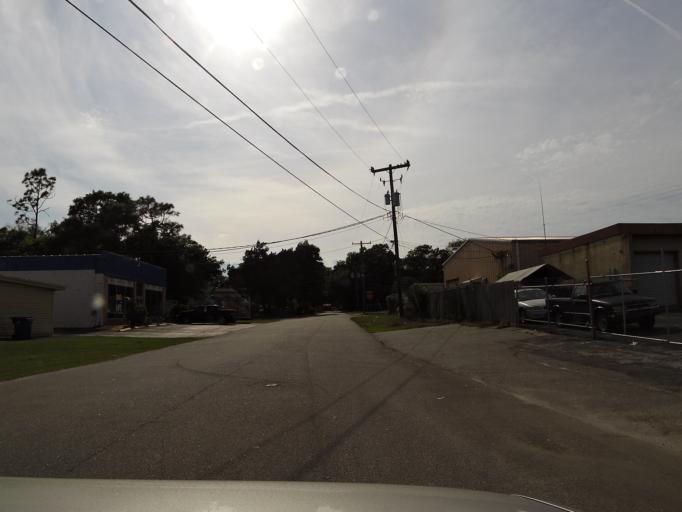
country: US
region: Florida
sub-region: Duval County
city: Jacksonville
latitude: 30.3325
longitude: -81.5891
